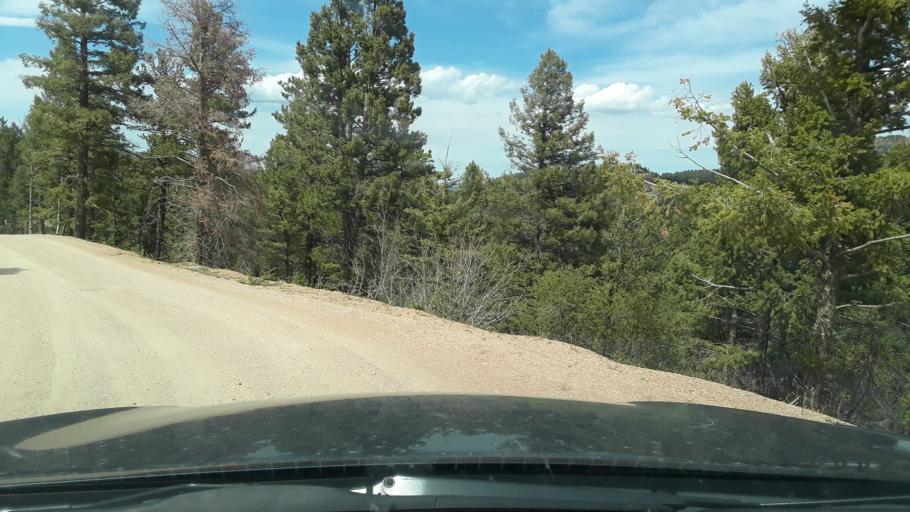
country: US
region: Colorado
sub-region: El Paso County
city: Palmer Lake
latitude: 39.0694
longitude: -104.9438
